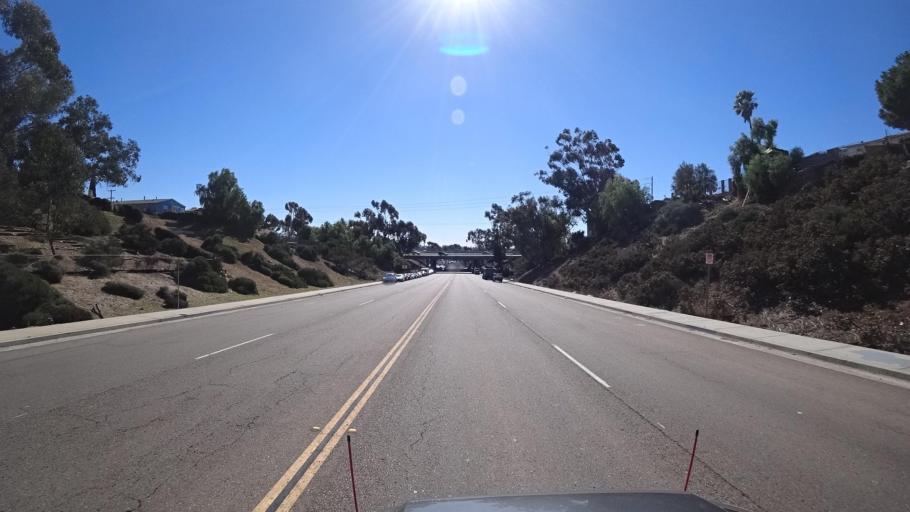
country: US
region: California
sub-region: San Diego County
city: Chula Vista
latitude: 32.6642
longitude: -117.0769
